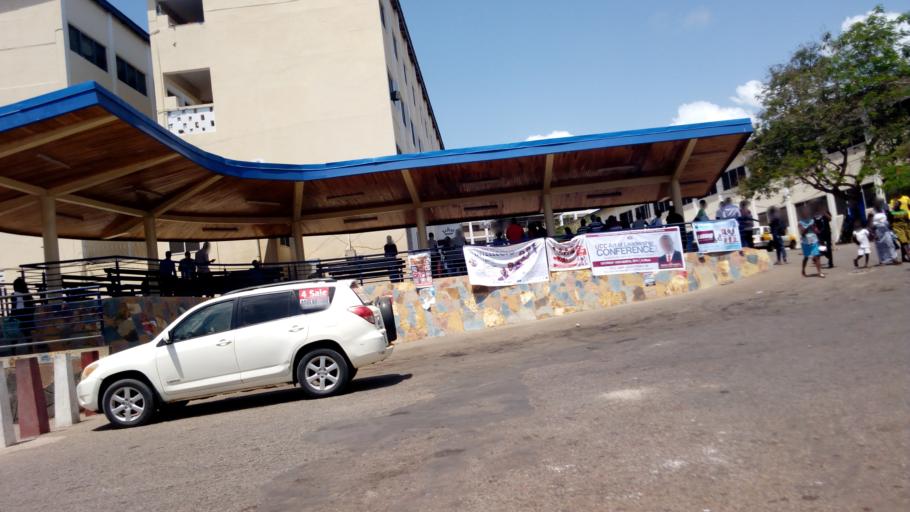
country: GH
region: Central
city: Cape Coast
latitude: 5.1054
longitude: -1.2857
